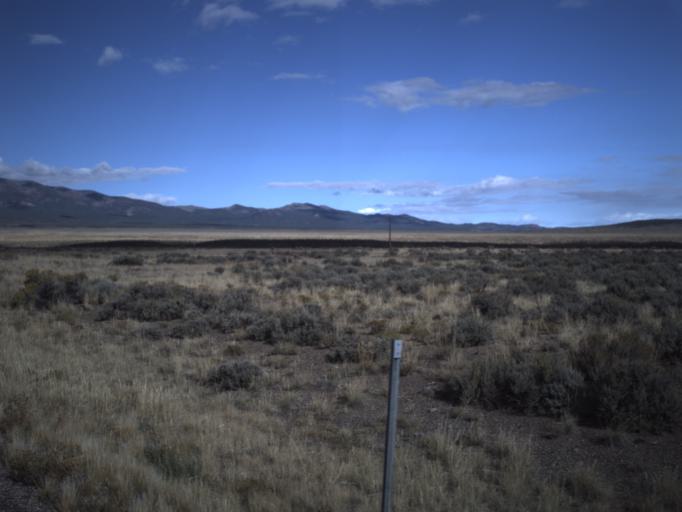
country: US
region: Utah
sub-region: Beaver County
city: Milford
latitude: 38.4373
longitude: -113.1456
